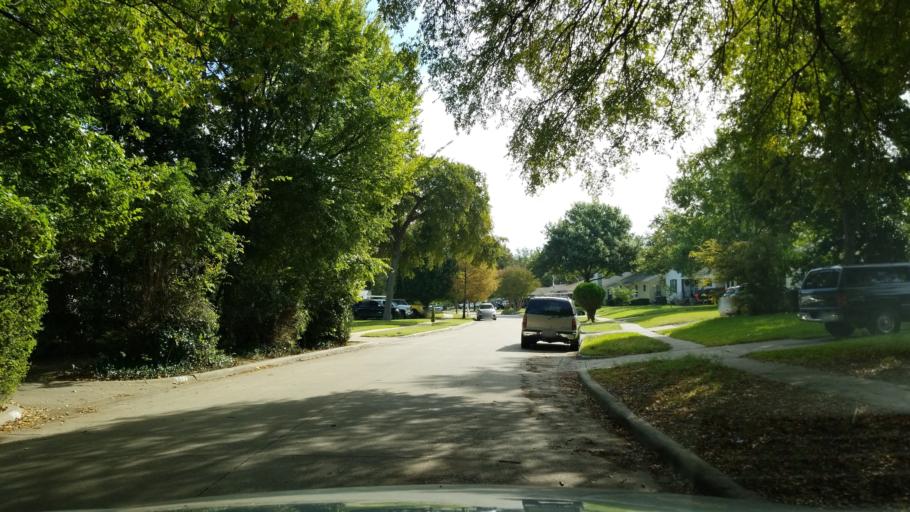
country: US
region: Texas
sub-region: Dallas County
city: Garland
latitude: 32.9032
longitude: -96.6514
